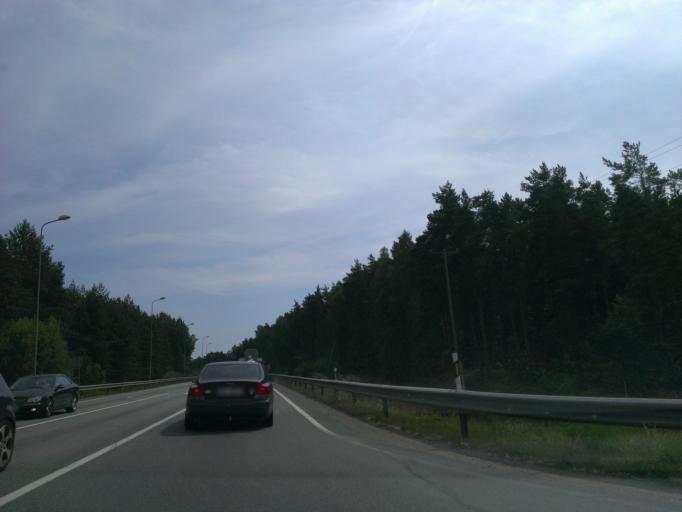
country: LV
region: Riga
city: Bergi
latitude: 56.9727
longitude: 24.3426
